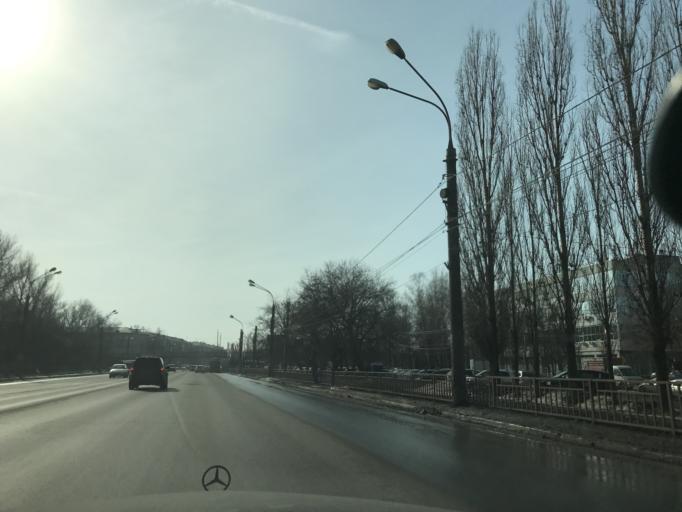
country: RU
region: Nizjnij Novgorod
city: Nizhniy Novgorod
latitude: 56.2702
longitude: 43.9169
